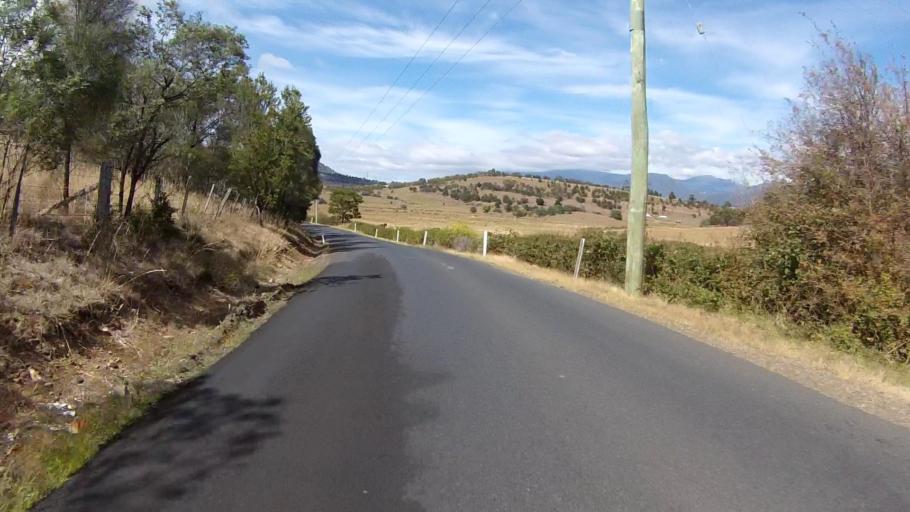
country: AU
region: Tasmania
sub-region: Brighton
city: Old Beach
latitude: -42.7481
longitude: 147.3005
